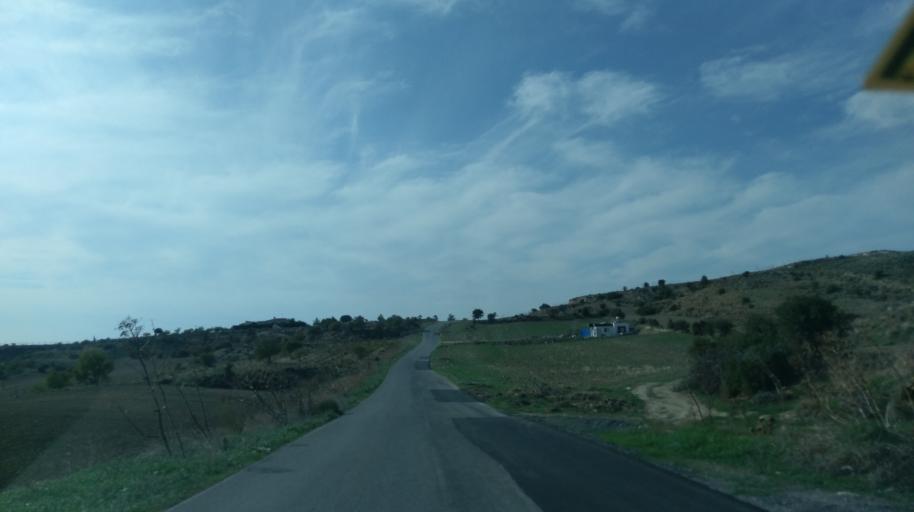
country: CY
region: Keryneia
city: Lapithos
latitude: 35.2827
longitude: 33.2342
